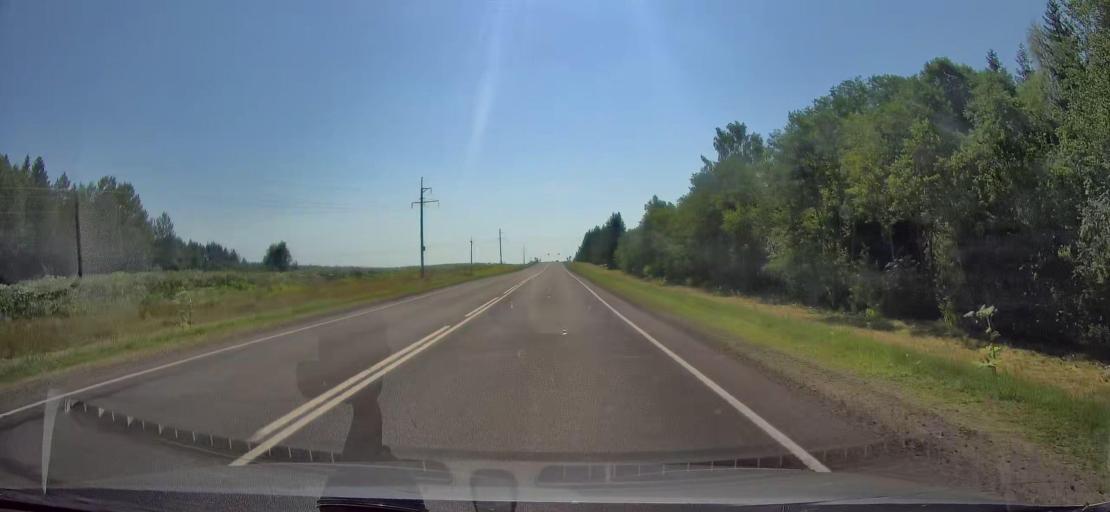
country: RU
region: Vologda
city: Chagoda
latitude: 59.0474
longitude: 35.3421
